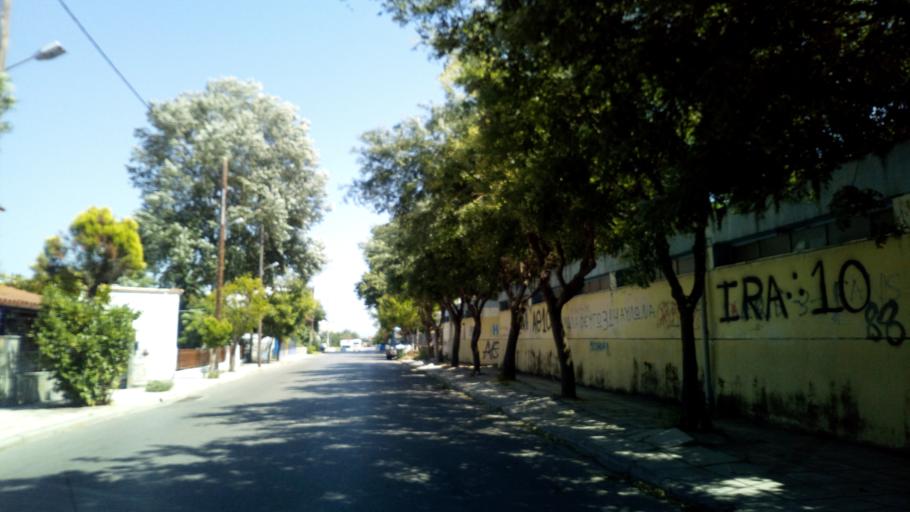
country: GR
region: Central Macedonia
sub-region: Nomos Thessalonikis
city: Lagkadas
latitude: 40.7483
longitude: 23.0714
